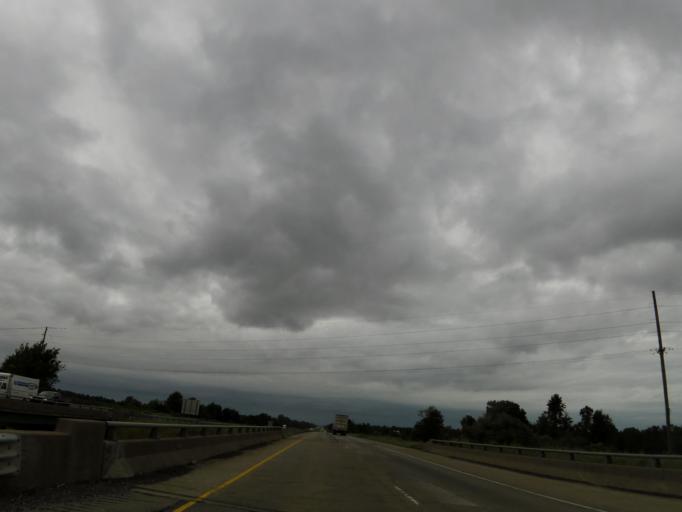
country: US
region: Illinois
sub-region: Massac County
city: Metropolis
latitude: 37.1907
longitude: -88.6851
